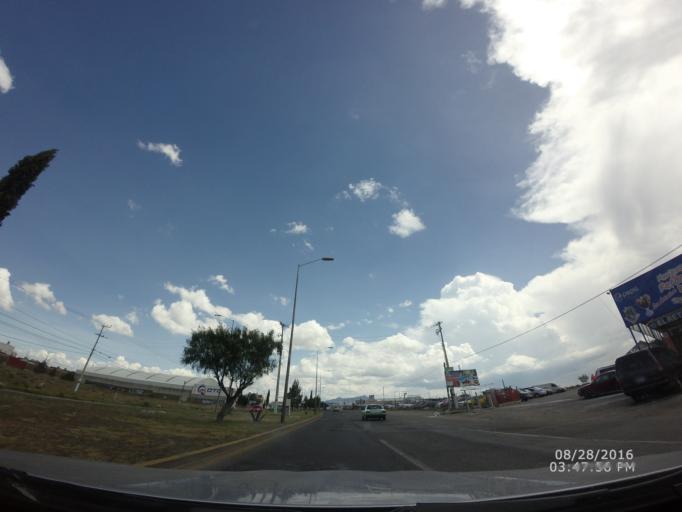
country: MX
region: Hidalgo
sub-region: Mineral de la Reforma
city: Nuevo Centro de Poblacion Agricola el Chacon
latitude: 20.0620
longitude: -98.7441
